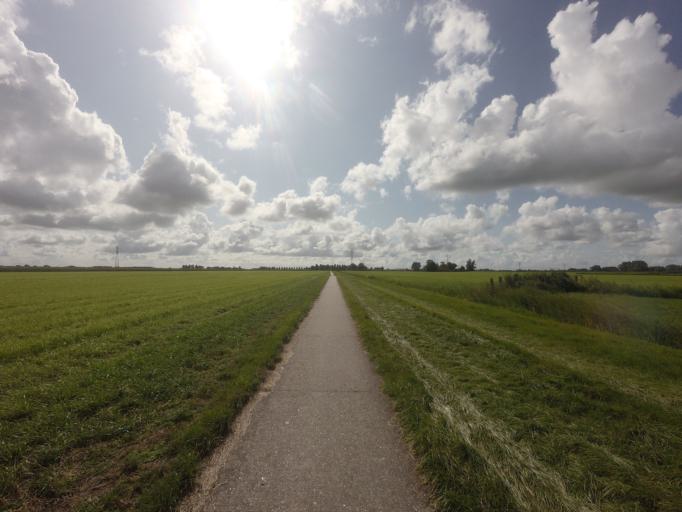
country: NL
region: Friesland
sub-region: Sudwest Fryslan
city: Sneek
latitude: 53.0660
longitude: 5.6377
